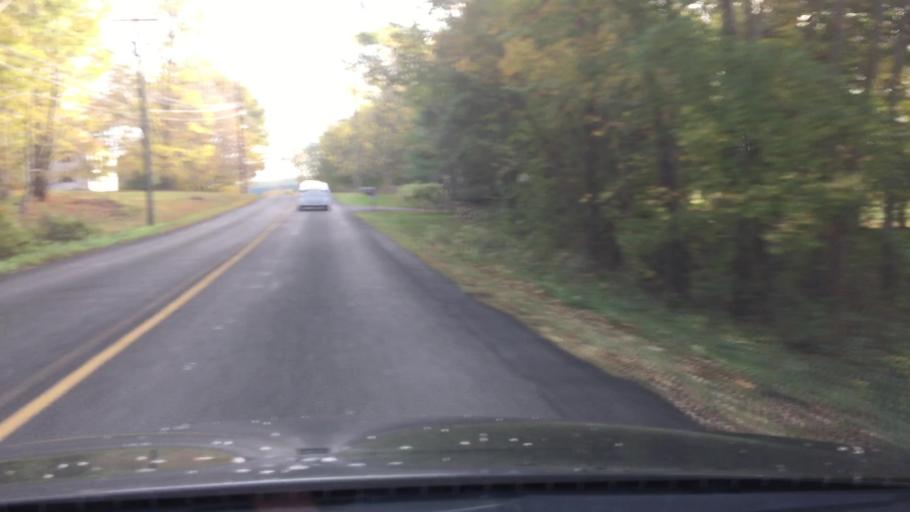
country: US
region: Connecticut
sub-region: Litchfield County
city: New Milford
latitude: 41.5527
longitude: -73.3150
